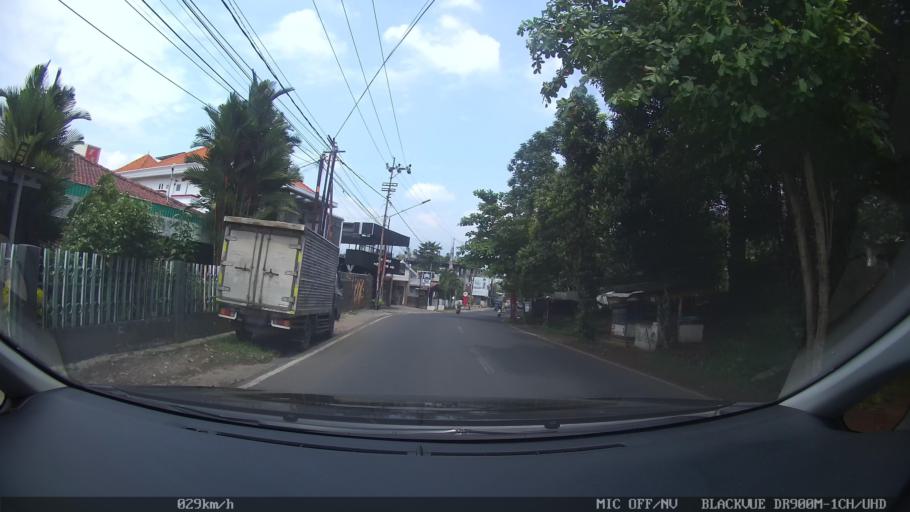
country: ID
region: Lampung
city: Bandarlampung
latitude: -5.4310
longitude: 105.2594
